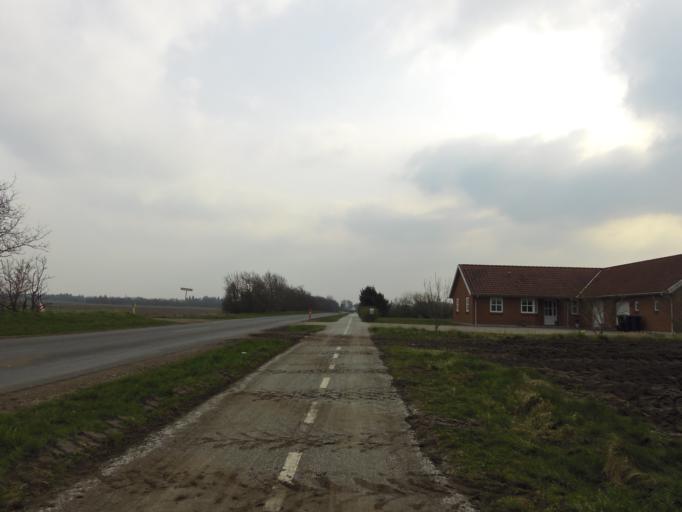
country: DK
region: South Denmark
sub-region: Esbjerg Kommune
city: Ribe
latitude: 55.3560
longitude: 8.7449
